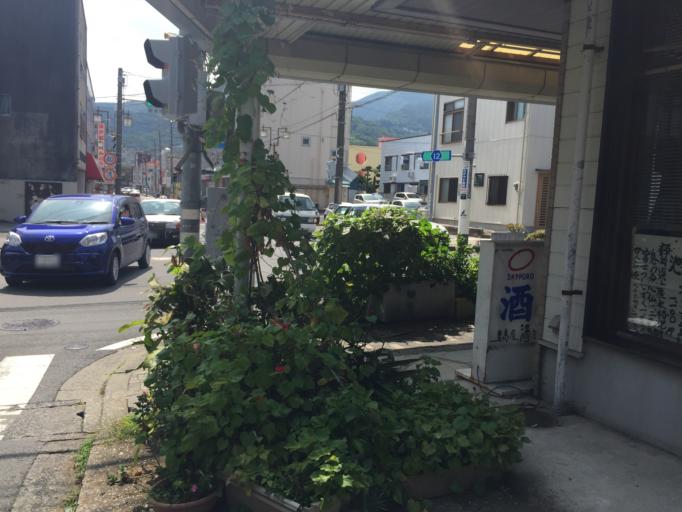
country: JP
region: Shizuoka
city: Ito
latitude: 34.9723
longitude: 139.0978
